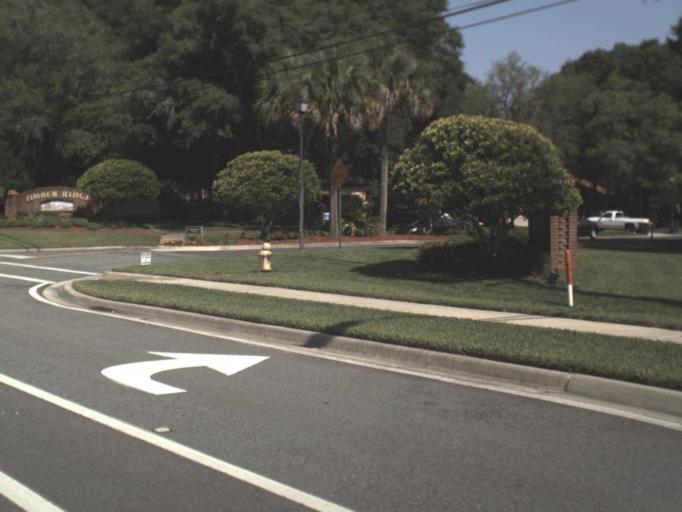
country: US
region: Florida
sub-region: Duval County
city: Neptune Beach
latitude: 30.2874
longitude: -81.4945
